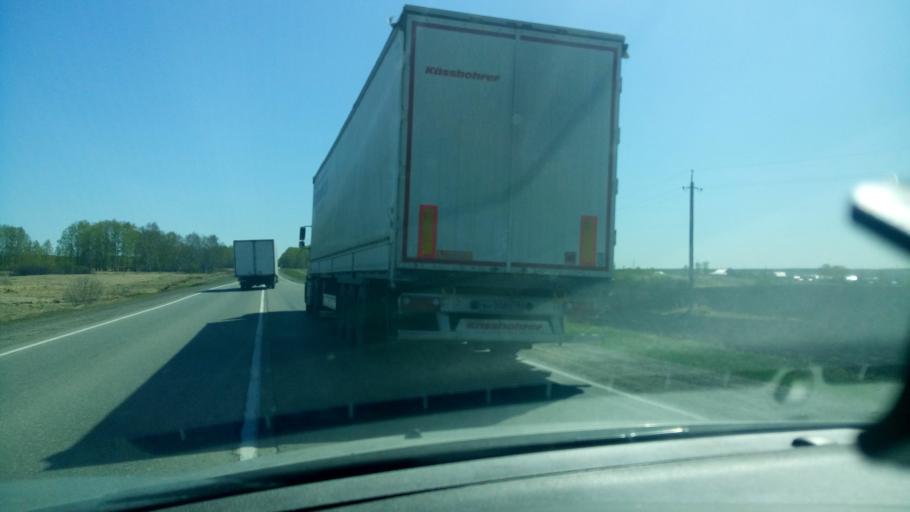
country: RU
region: Sverdlovsk
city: Bogdanovich
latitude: 56.7556
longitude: 62.2164
